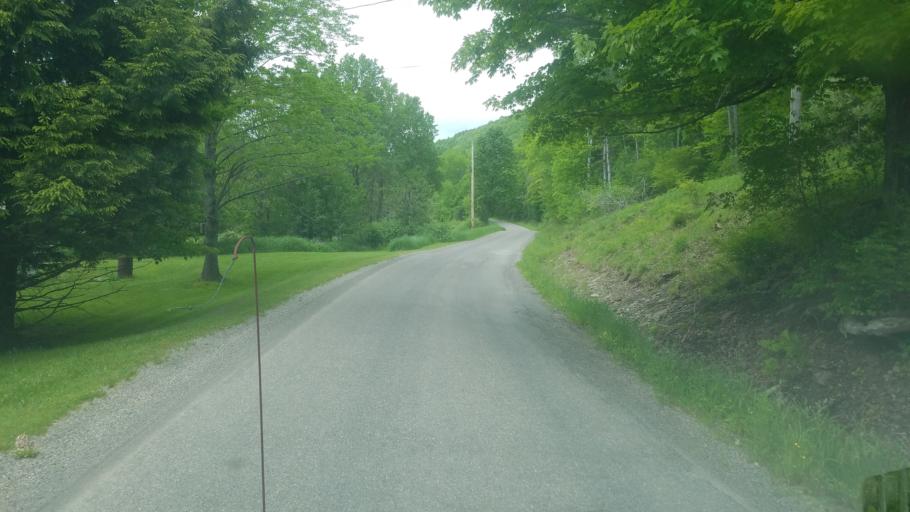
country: US
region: Pennsylvania
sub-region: Tioga County
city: Westfield
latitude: 41.8880
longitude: -77.5990
